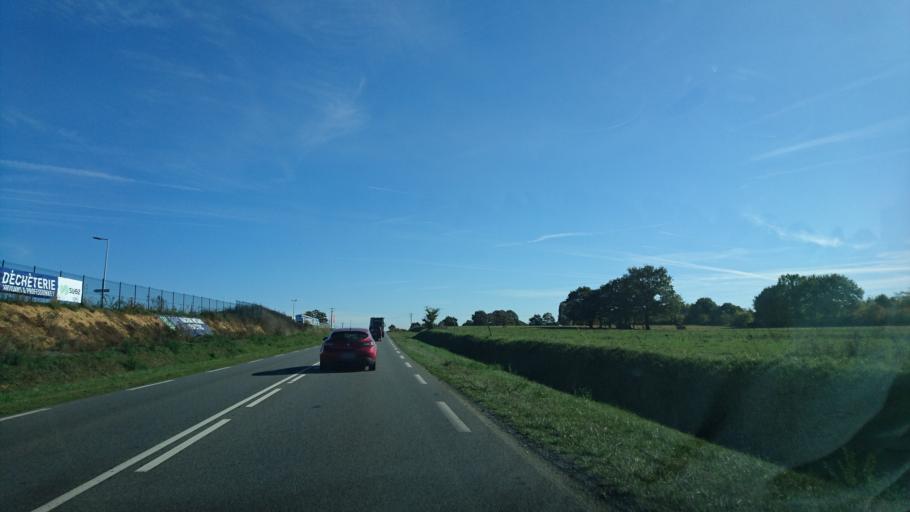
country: FR
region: Brittany
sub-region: Departement d'Ille-et-Vilaine
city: Saint-Jacques-de-la-Lande
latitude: 48.0532
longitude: -1.7248
